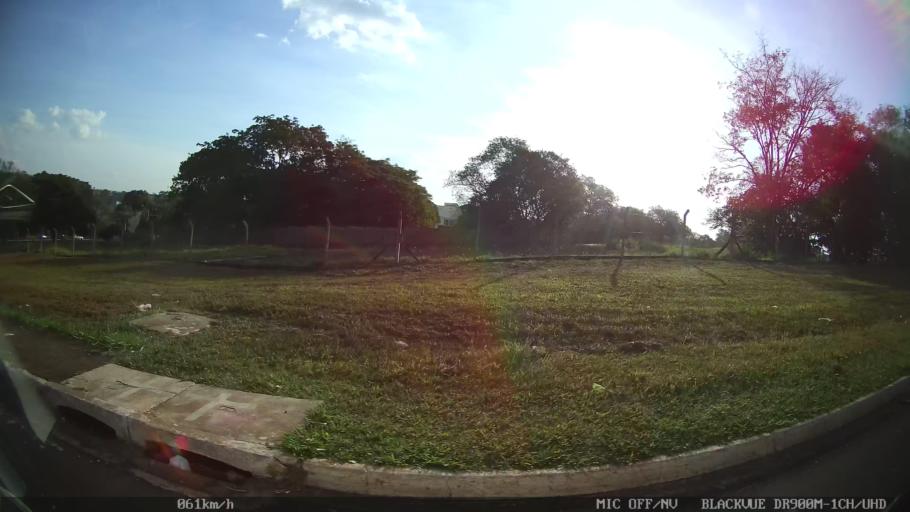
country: BR
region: Sao Paulo
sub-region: Ribeirao Preto
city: Ribeirao Preto
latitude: -21.1716
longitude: -47.8439
